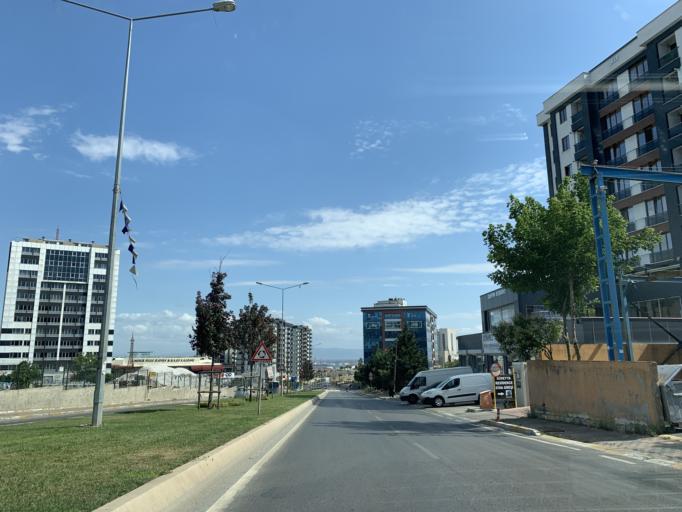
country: TR
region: Istanbul
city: Pendik
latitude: 40.8930
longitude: 29.2623
